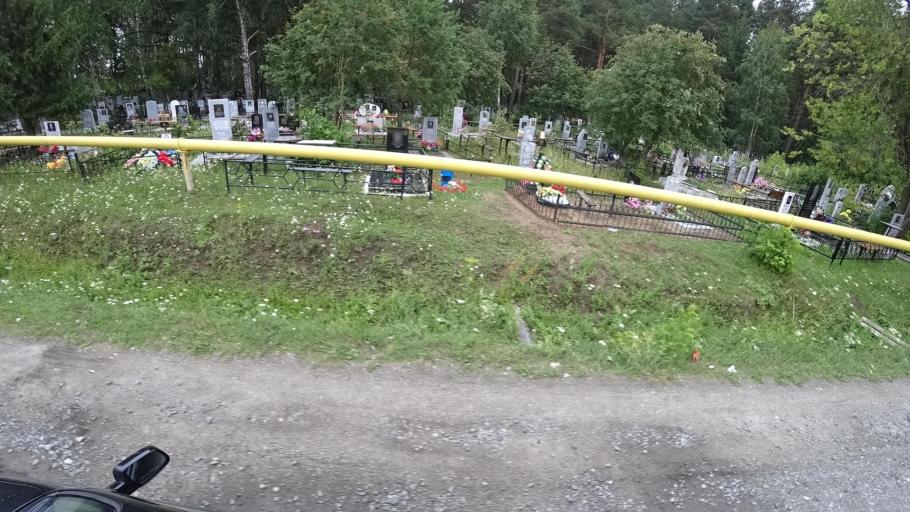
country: RU
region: Sverdlovsk
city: Kamyshlov
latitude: 56.8423
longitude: 62.7535
